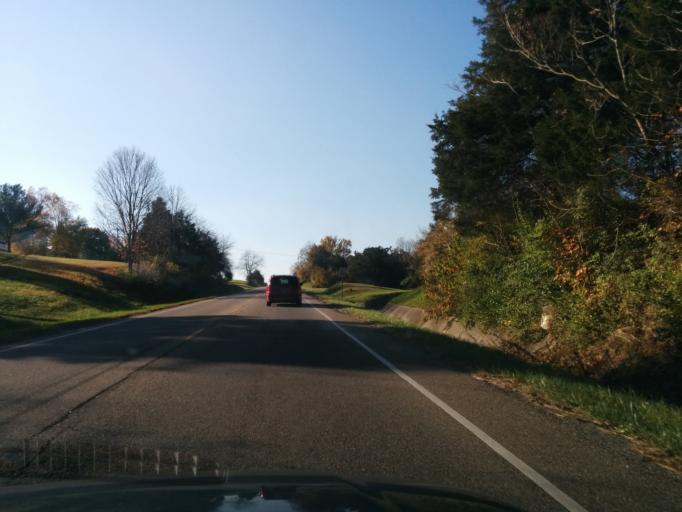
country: US
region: Virginia
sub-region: Rockbridge County
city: East Lexington
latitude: 37.7870
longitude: -79.4298
